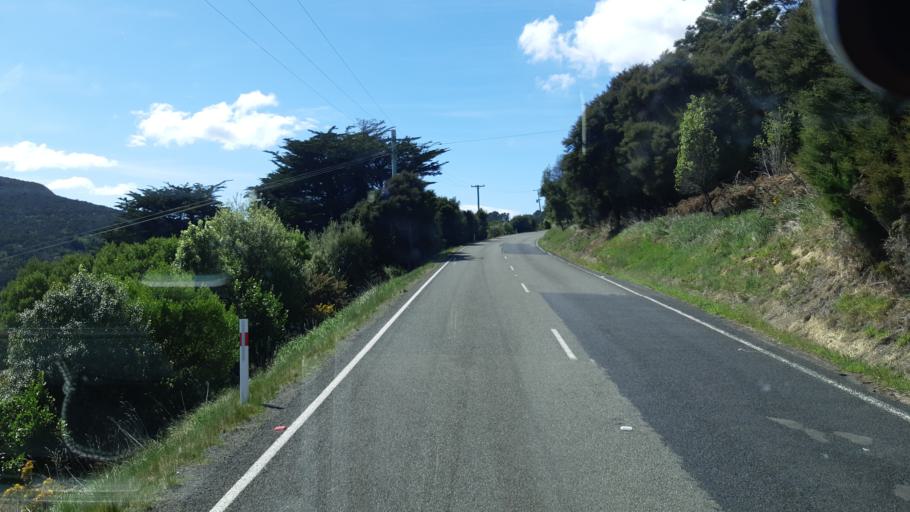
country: NZ
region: Otago
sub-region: Dunedin City
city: Portobello
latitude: -45.7769
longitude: 170.5898
